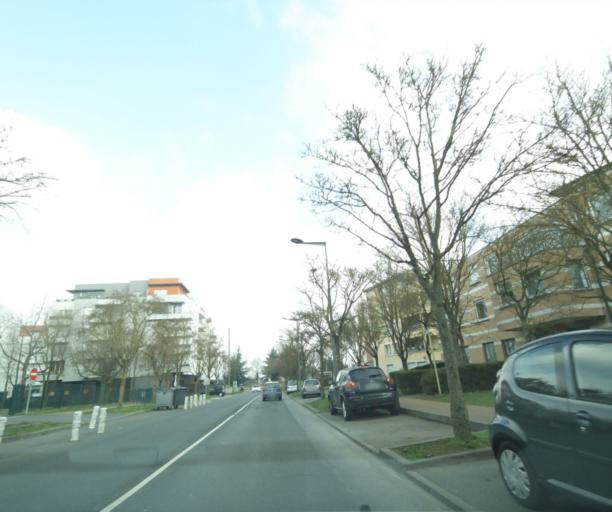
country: FR
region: Ile-de-France
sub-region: Departement du Val-d'Oise
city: Vaureal
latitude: 49.0514
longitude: 2.0380
